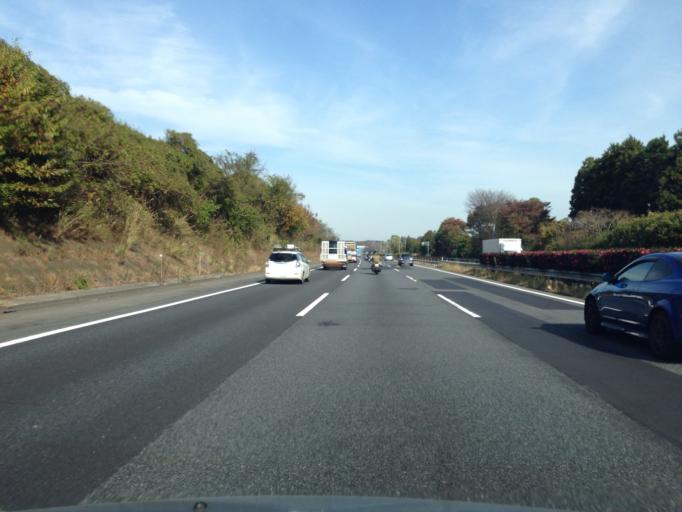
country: JP
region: Ibaraki
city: Ishioka
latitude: 36.1408
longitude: 140.2061
